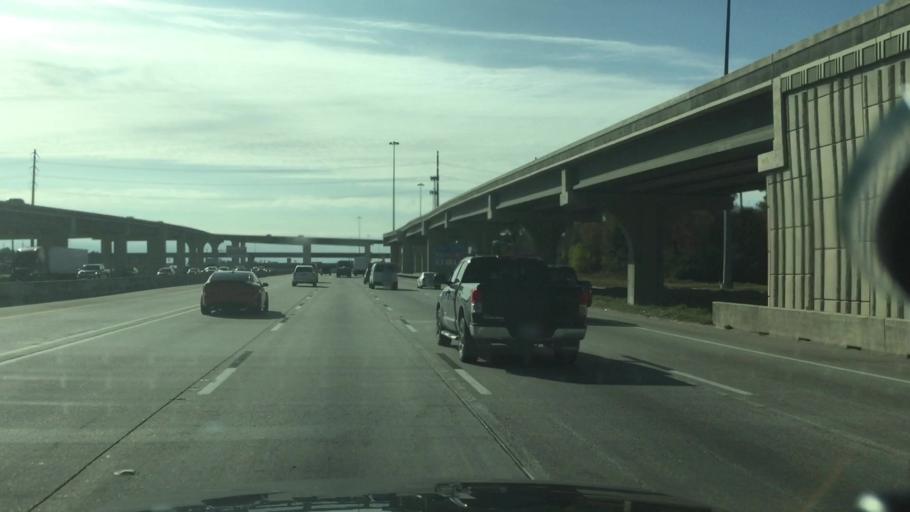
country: US
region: Texas
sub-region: Harris County
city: Spring
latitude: 30.0986
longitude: -95.4362
